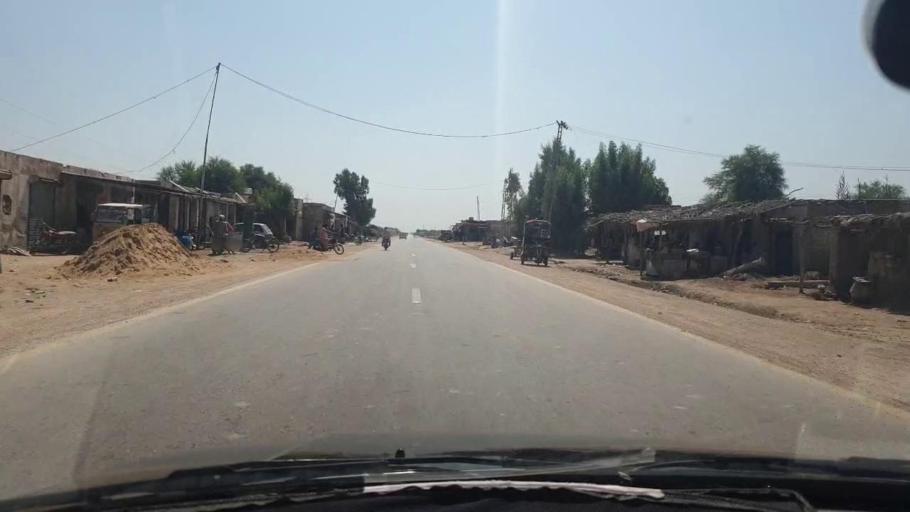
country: PK
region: Sindh
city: Chambar
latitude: 25.3572
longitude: 68.7875
